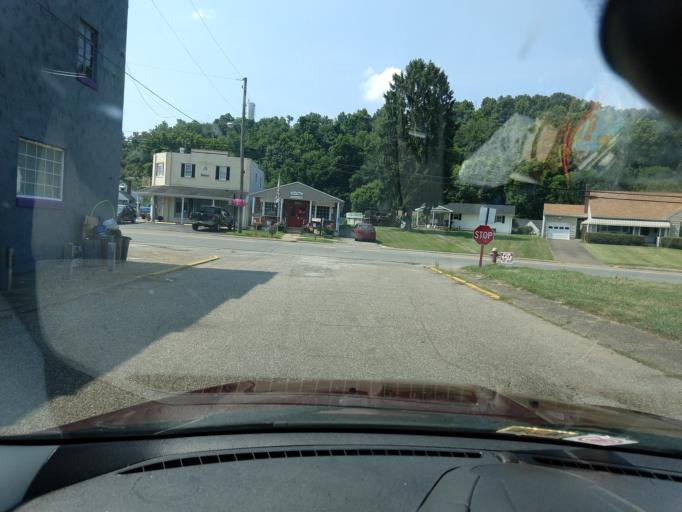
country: US
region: West Virginia
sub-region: Mason County
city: New Haven
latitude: 38.9873
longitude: -81.9748
